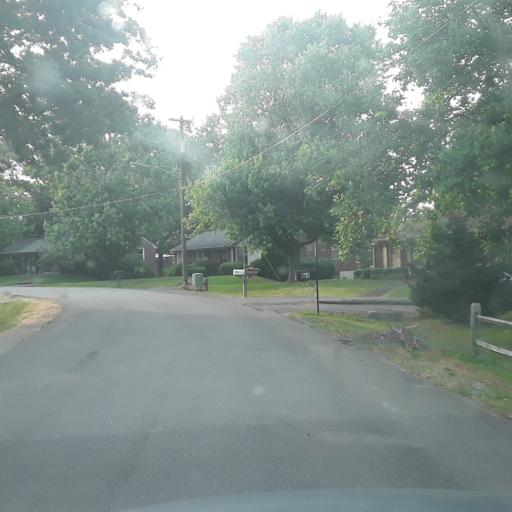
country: US
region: Tennessee
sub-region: Davidson County
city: Oak Hill
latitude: 36.0800
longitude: -86.7538
